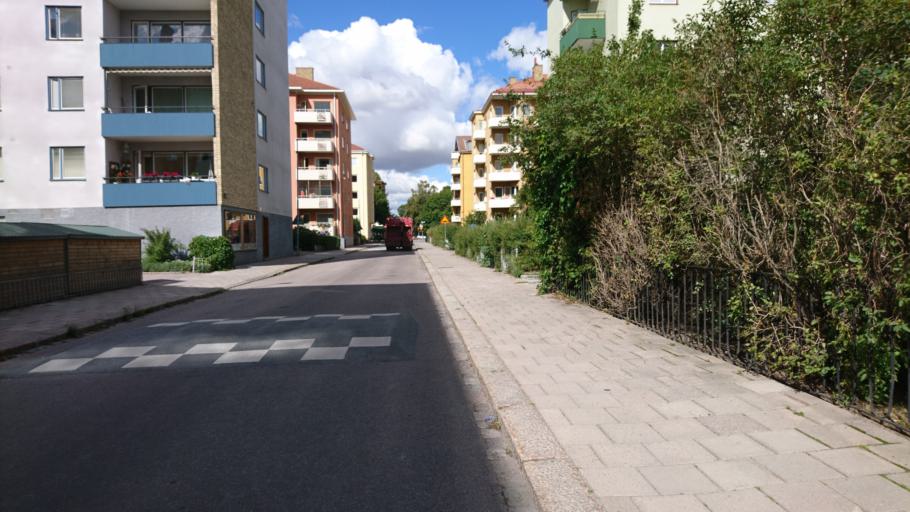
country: SE
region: Uppsala
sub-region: Uppsala Kommun
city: Uppsala
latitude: 59.8632
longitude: 17.6284
